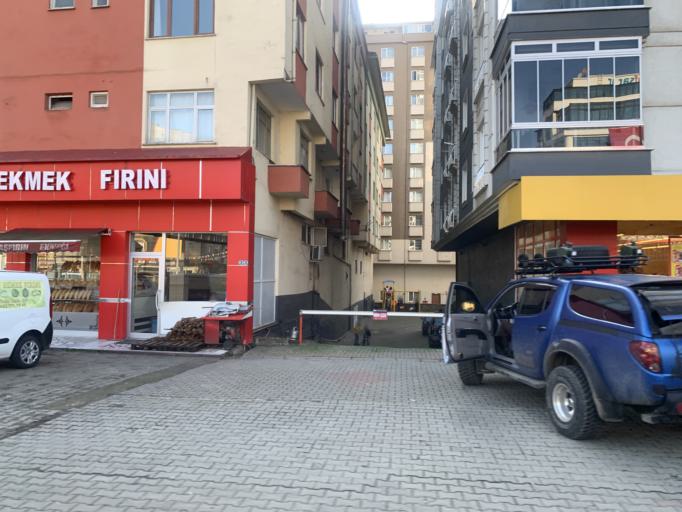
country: TR
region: Trabzon
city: Of
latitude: 40.9433
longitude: 40.2629
